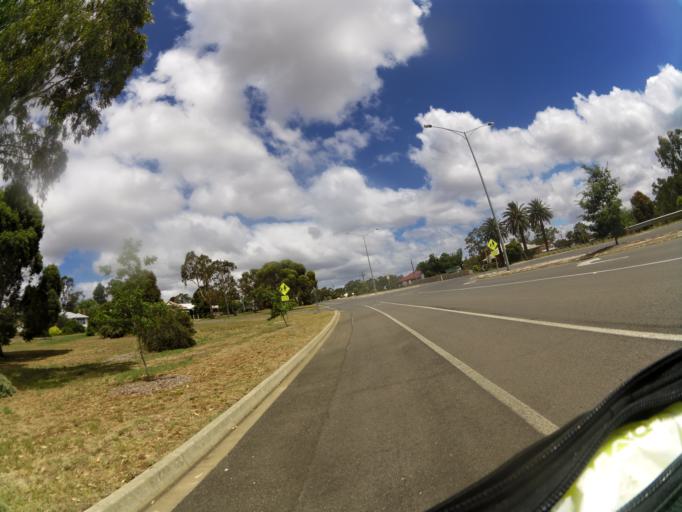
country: AU
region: Victoria
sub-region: Mount Alexander
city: Castlemaine
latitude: -36.9990
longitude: 144.2604
